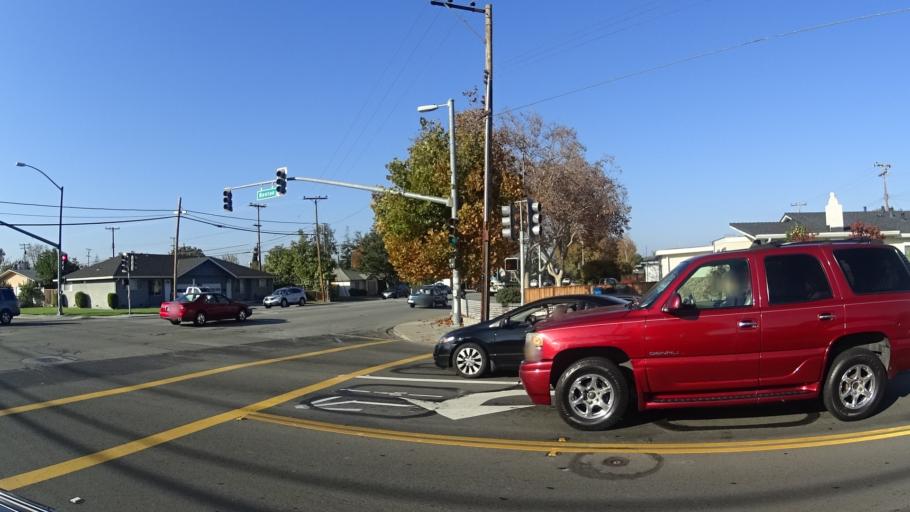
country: US
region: California
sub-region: Santa Clara County
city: Santa Clara
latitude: 37.3465
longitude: -121.9775
